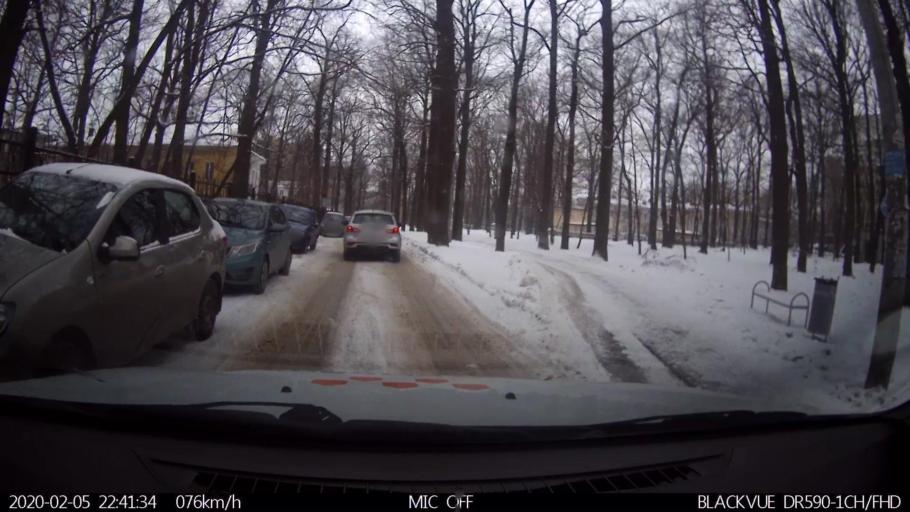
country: RU
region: Nizjnij Novgorod
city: Imeni Stepana Razina
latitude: 54.7205
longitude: 44.3404
